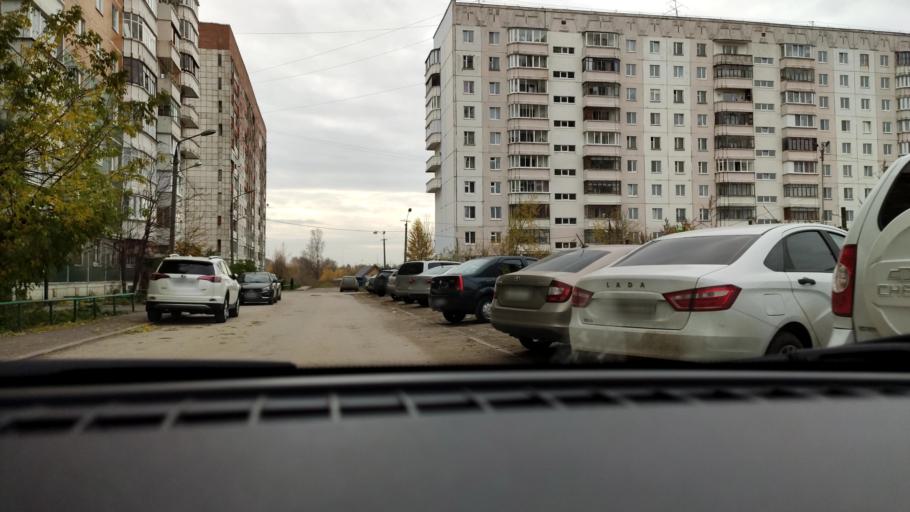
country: RU
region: Perm
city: Perm
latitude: 58.0599
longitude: 56.3442
